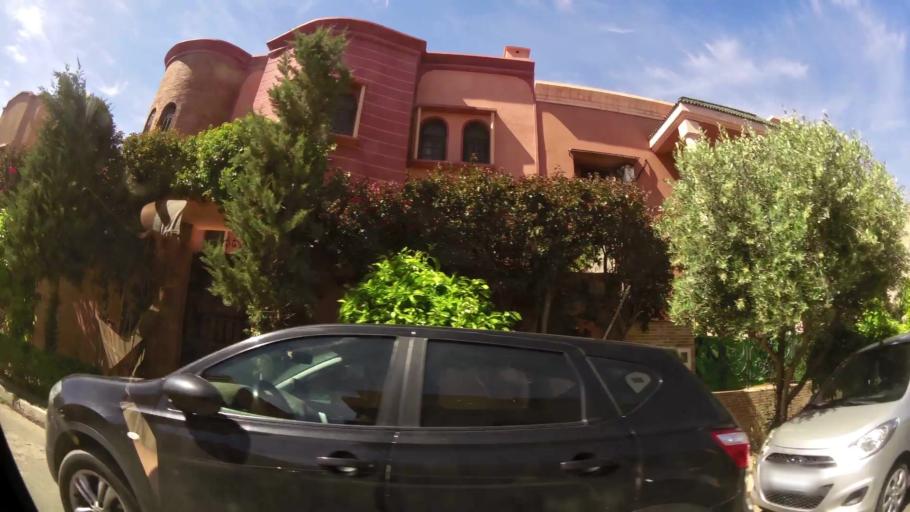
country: MA
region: Marrakech-Tensift-Al Haouz
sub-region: Marrakech
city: Marrakesh
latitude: 31.6799
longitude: -8.0044
